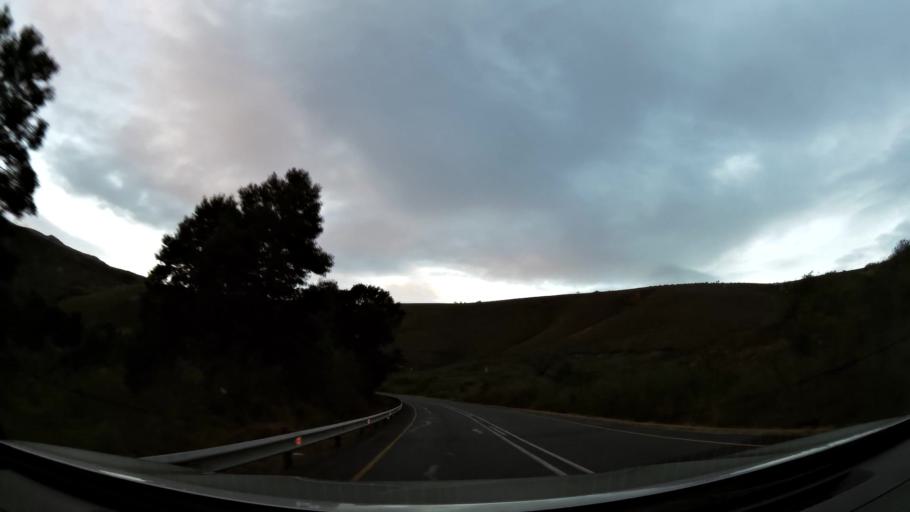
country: ZA
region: Western Cape
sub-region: Overberg District Municipality
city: Swellendam
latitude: -33.9895
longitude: 20.7142
